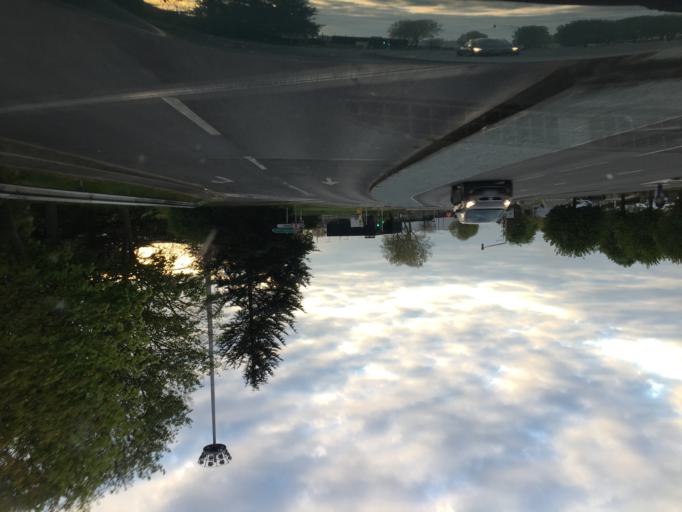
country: FR
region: Centre
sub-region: Departement du Loiret
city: Saint-Jean-de-la-Ruelle
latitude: 47.9061
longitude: 1.8703
